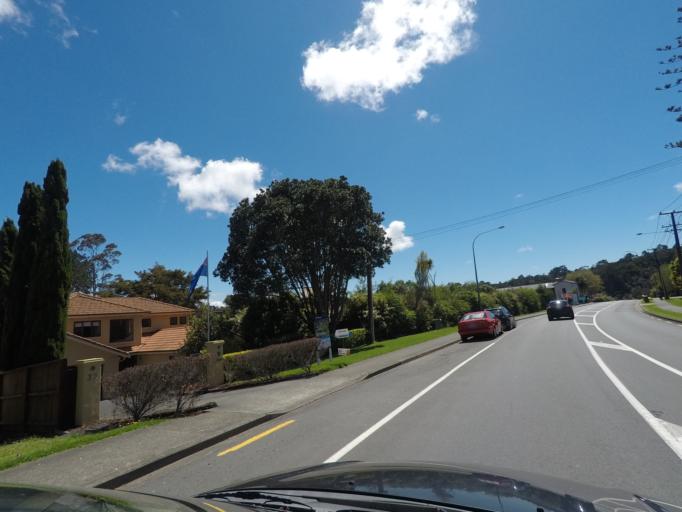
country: NZ
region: Auckland
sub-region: Auckland
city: Rothesay Bay
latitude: -36.7252
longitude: 174.6883
